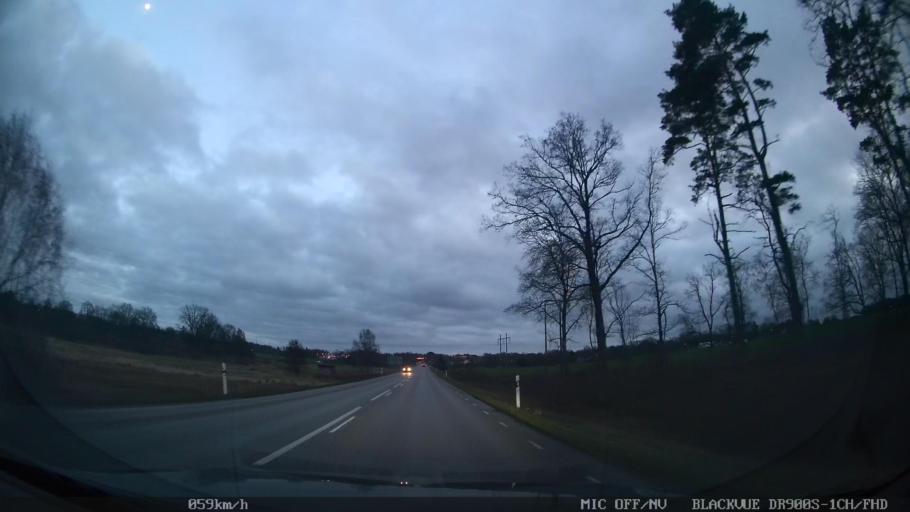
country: SE
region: Skane
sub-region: Hassleholms Kommun
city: Hassleholm
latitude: 56.1777
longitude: 13.7558
